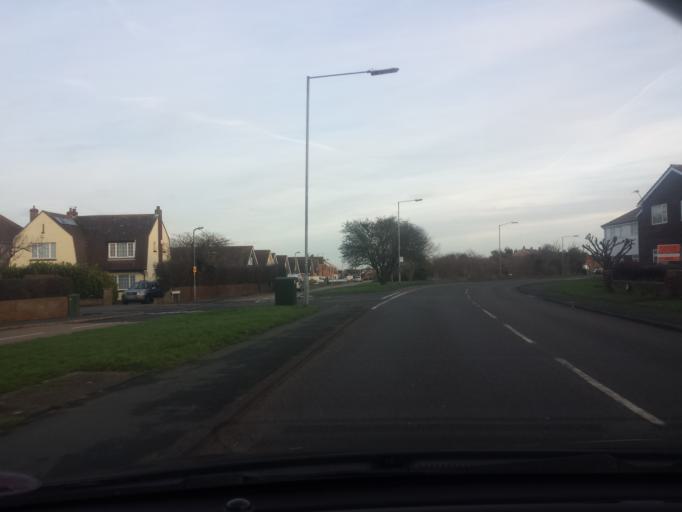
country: GB
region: England
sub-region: Essex
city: Clacton-on-Sea
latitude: 51.8064
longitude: 1.1957
